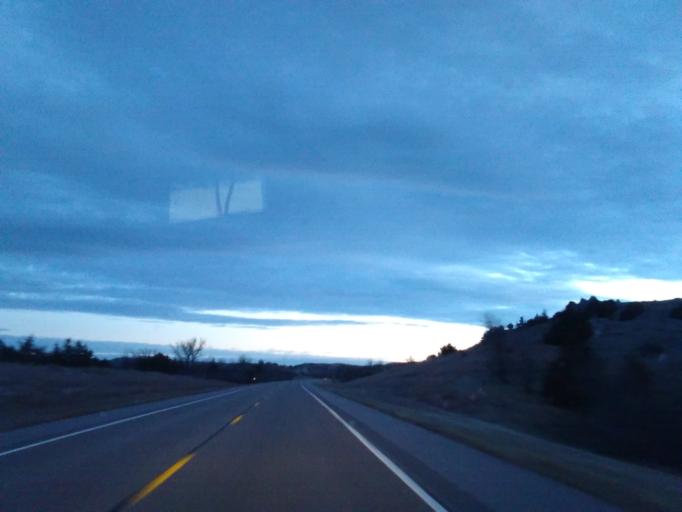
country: US
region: Nebraska
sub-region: Garden County
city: Oshkosh
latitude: 41.2844
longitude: -102.1184
